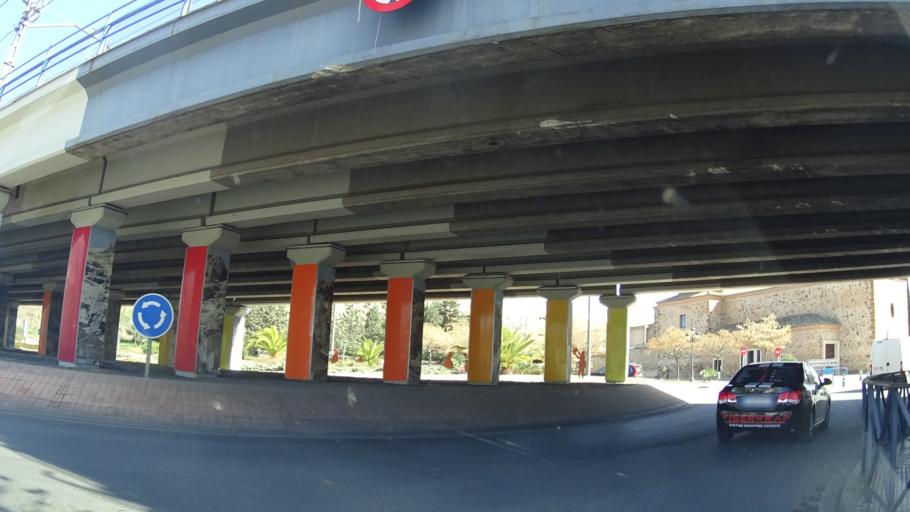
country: ES
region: Castille-La Mancha
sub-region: Provincia de Ciudad Real
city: Puertollano
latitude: 38.6943
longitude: -4.1096
